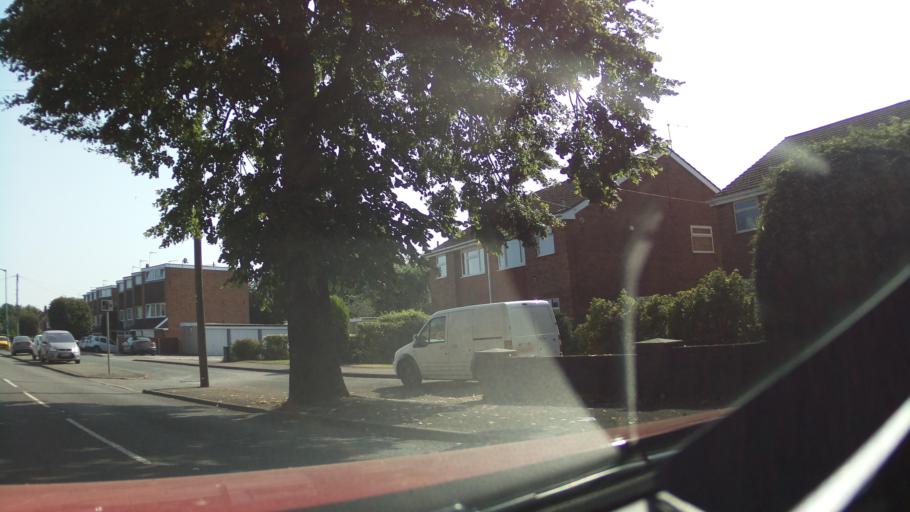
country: GB
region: England
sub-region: Staffordshire
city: Lichfield
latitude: 52.6862
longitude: -1.8096
